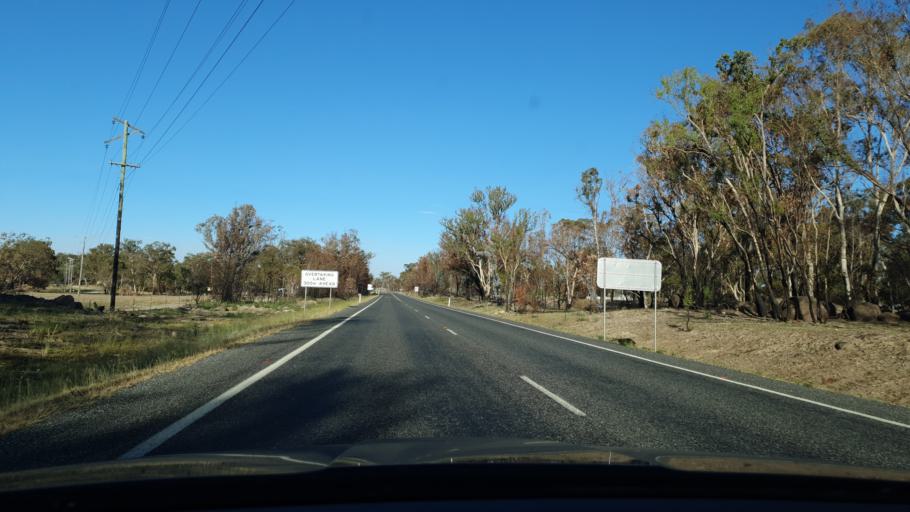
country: AU
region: Queensland
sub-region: Southern Downs
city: Stanthorpe
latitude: -28.6394
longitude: 151.9432
